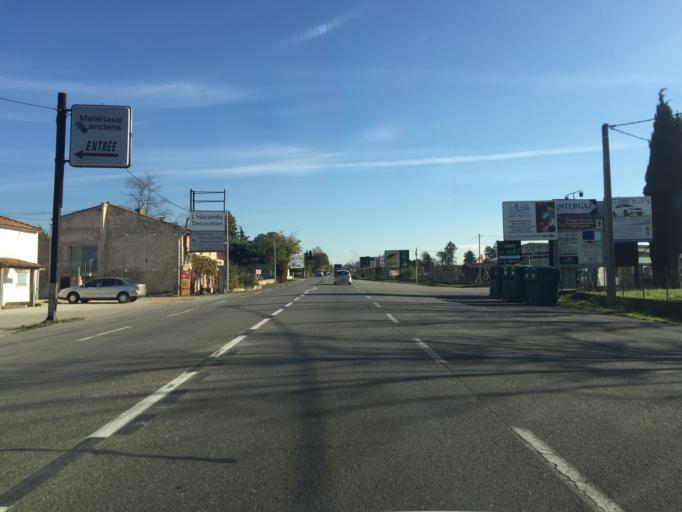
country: FR
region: Provence-Alpes-Cote d'Azur
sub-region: Departement des Bouches-du-Rhone
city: Eguilles
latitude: 43.5798
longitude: 5.3800
